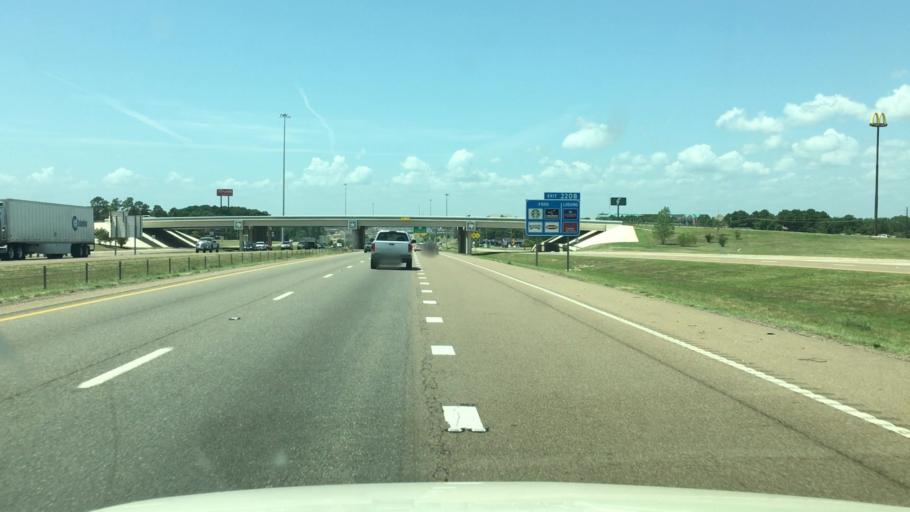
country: US
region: Arkansas
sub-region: Miller County
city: Texarkana
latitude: 33.4666
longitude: -94.0643
